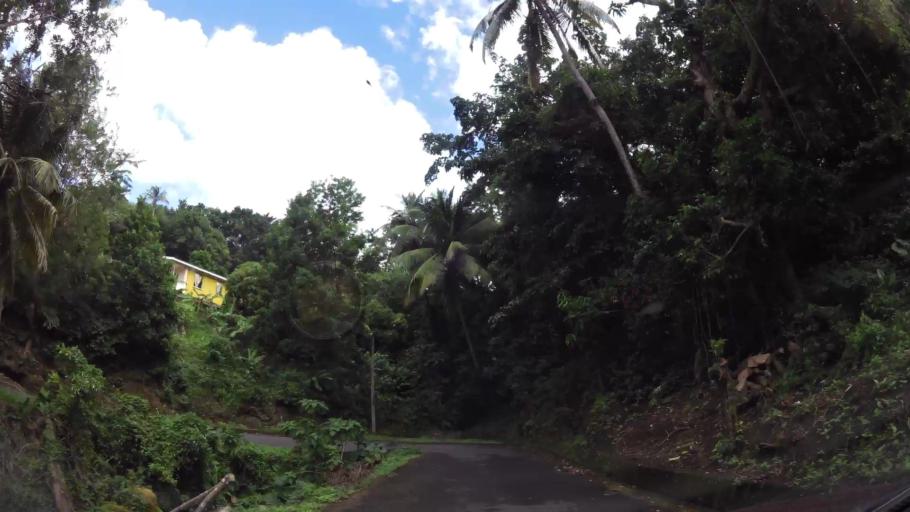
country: DM
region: Saint John
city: Portsmouth
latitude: 15.6165
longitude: -61.4627
